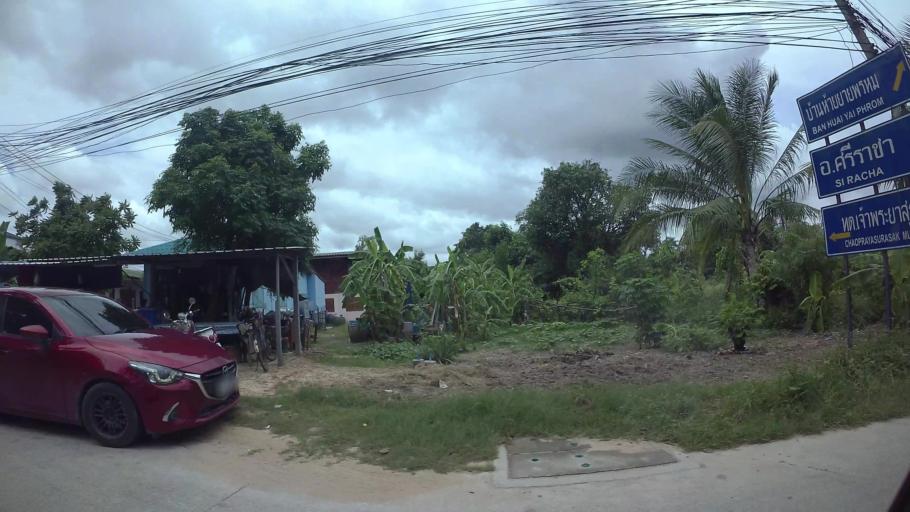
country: TH
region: Chon Buri
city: Si Racha
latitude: 13.1608
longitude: 100.9738
